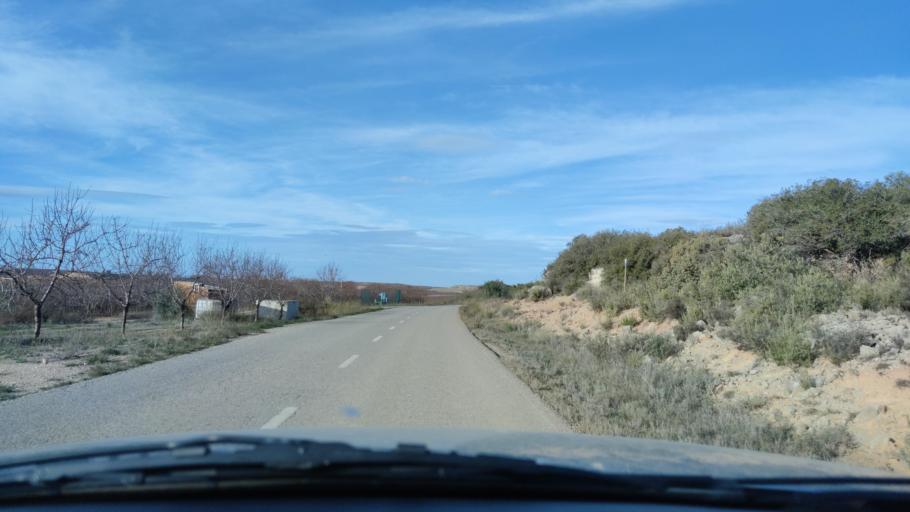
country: ES
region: Catalonia
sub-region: Provincia de Lleida
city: Alcano
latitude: 41.4683
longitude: 0.6439
